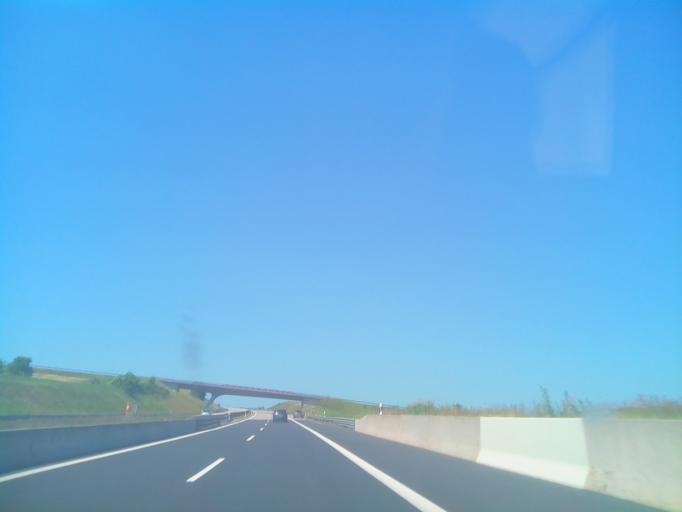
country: DE
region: Bavaria
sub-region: Regierungsbezirk Unterfranken
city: Hollstadt
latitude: 50.3529
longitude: 10.3168
